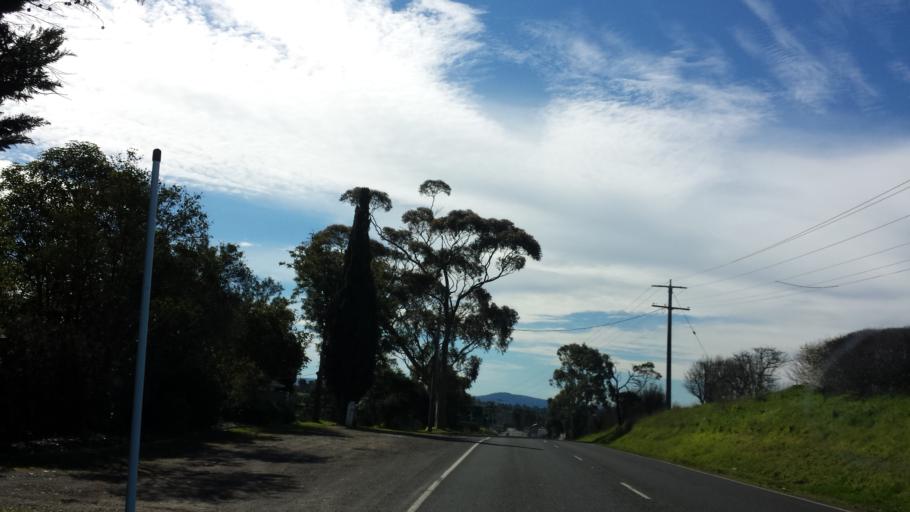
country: AU
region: Victoria
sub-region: Nillumbik
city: Research
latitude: -37.6904
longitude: 145.2159
